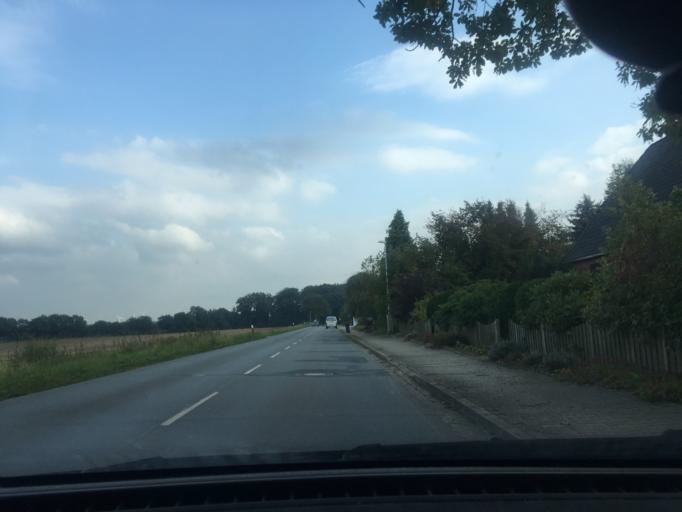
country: DE
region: Lower Saxony
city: Rullstorf
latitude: 53.2719
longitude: 10.5134
